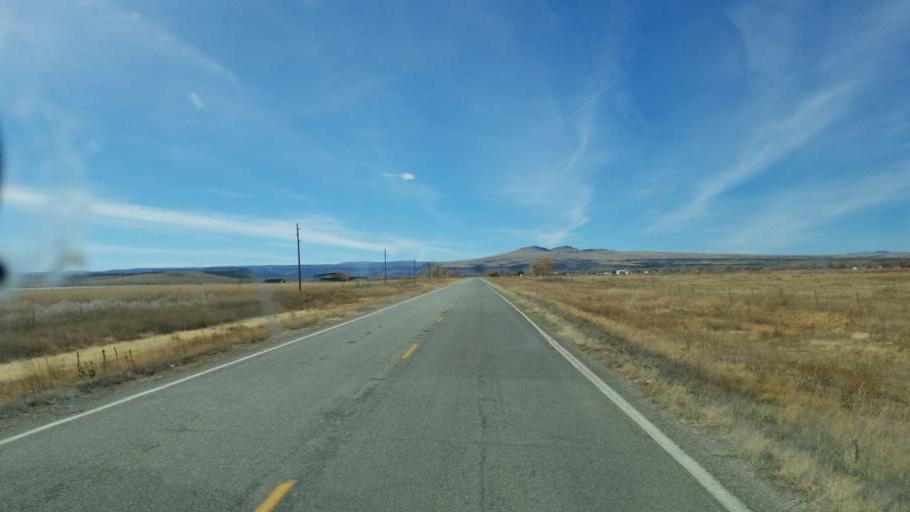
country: US
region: Colorado
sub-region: Conejos County
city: Conejos
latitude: 37.0646
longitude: -106.0394
